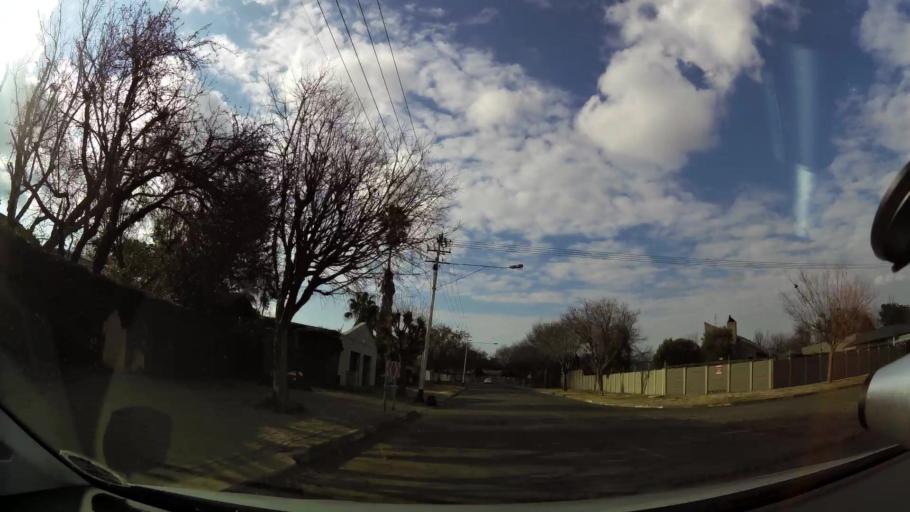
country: ZA
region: Orange Free State
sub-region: Mangaung Metropolitan Municipality
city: Bloemfontein
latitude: -29.0819
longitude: 26.2112
